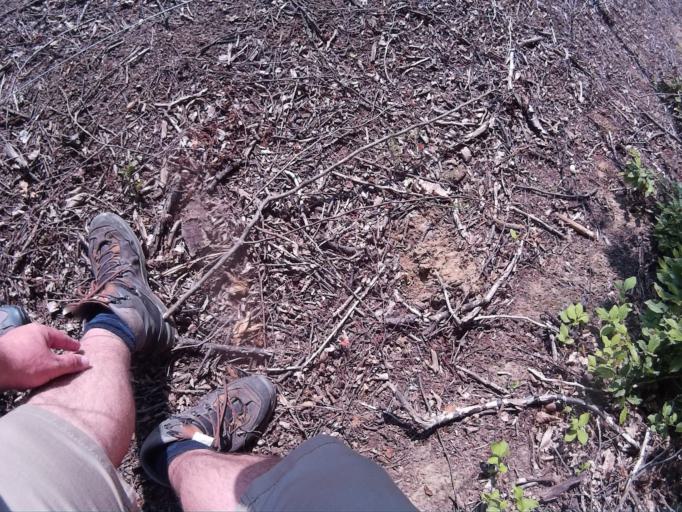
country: AT
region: Burgenland
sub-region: Politischer Bezirk Gussing
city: Heiligenbrunn
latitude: 46.9287
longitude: 16.4675
